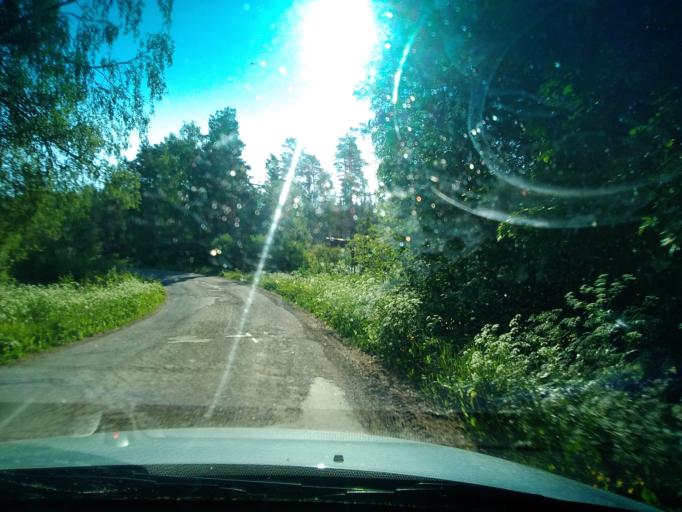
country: FI
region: Haeme
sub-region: Forssa
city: Tammela
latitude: 60.7720
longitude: 23.8090
